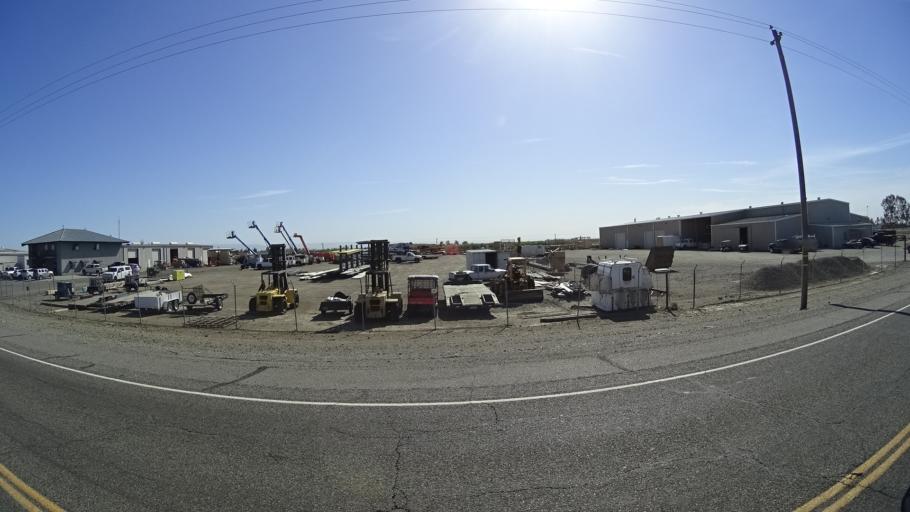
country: US
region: California
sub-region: Glenn County
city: Orland
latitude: 39.6913
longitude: -122.1968
